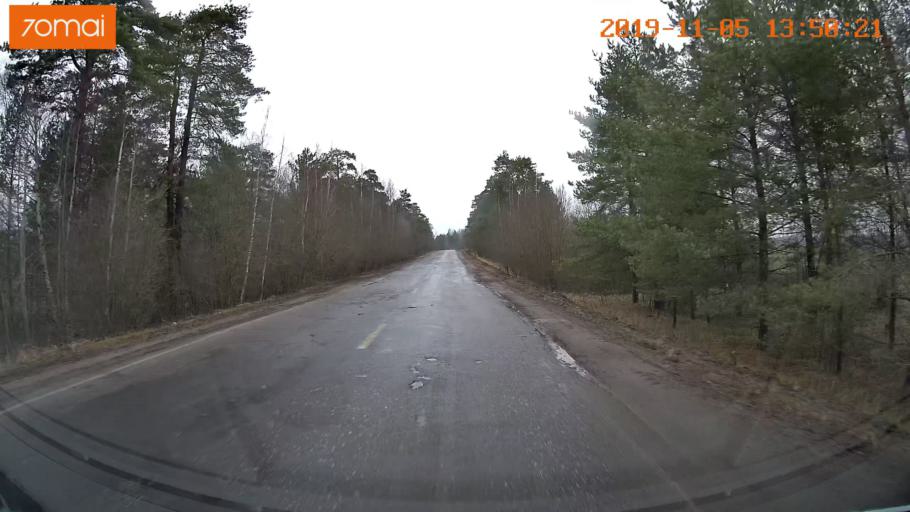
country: RU
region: Ivanovo
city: Kaminskiy
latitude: 57.0187
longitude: 41.4084
